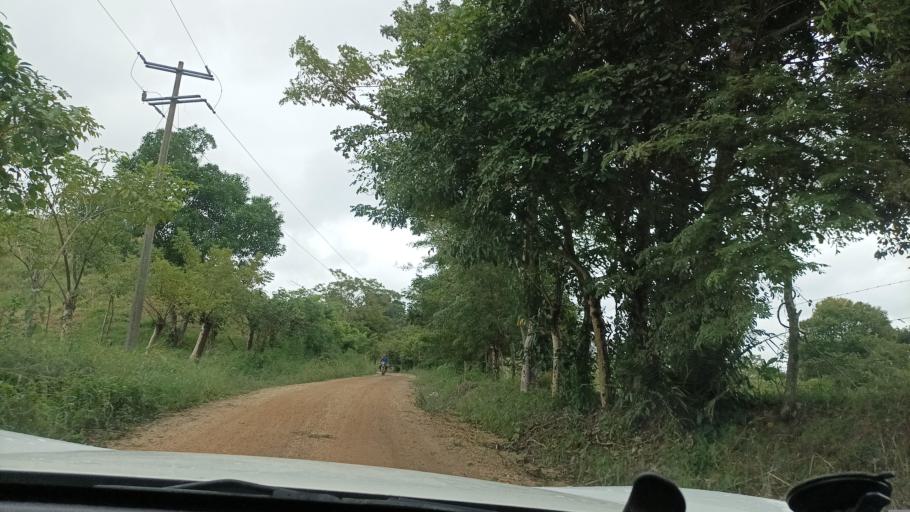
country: MX
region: Veracruz
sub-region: Moloacan
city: Cuichapa
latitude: 17.7953
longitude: -94.3804
